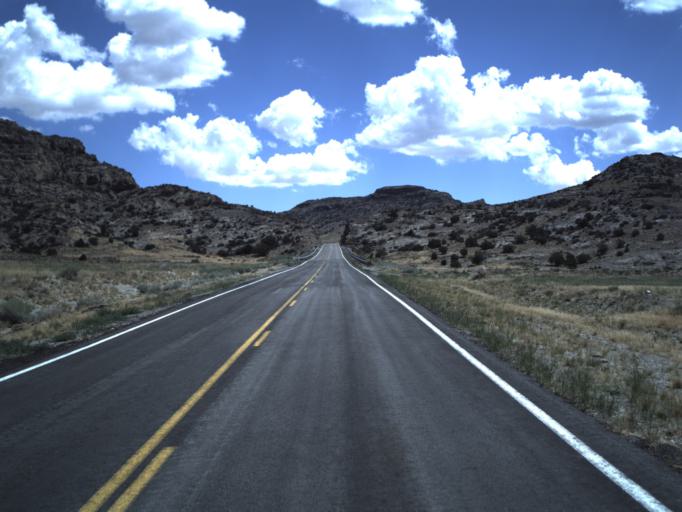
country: US
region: Utah
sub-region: Beaver County
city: Milford
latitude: 39.0724
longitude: -113.6623
